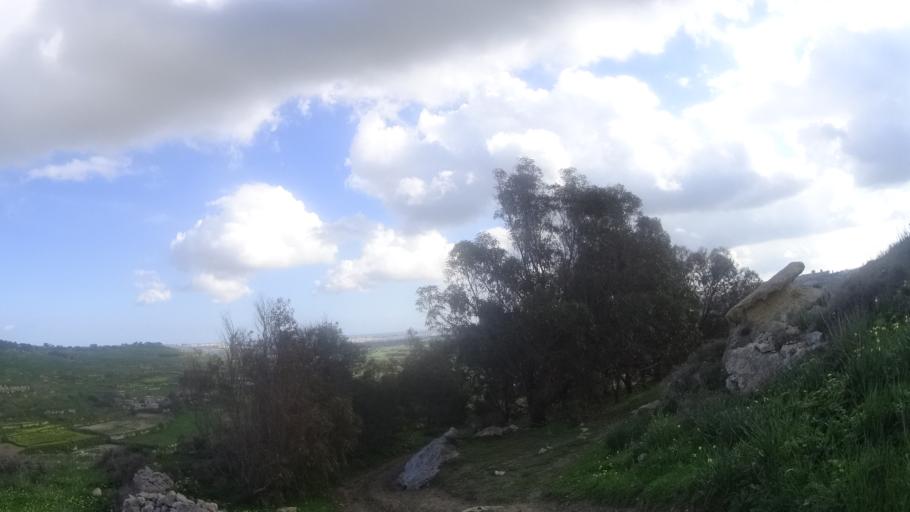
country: MT
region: L-Imtarfa
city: Imtarfa
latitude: 35.8995
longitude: 14.3855
